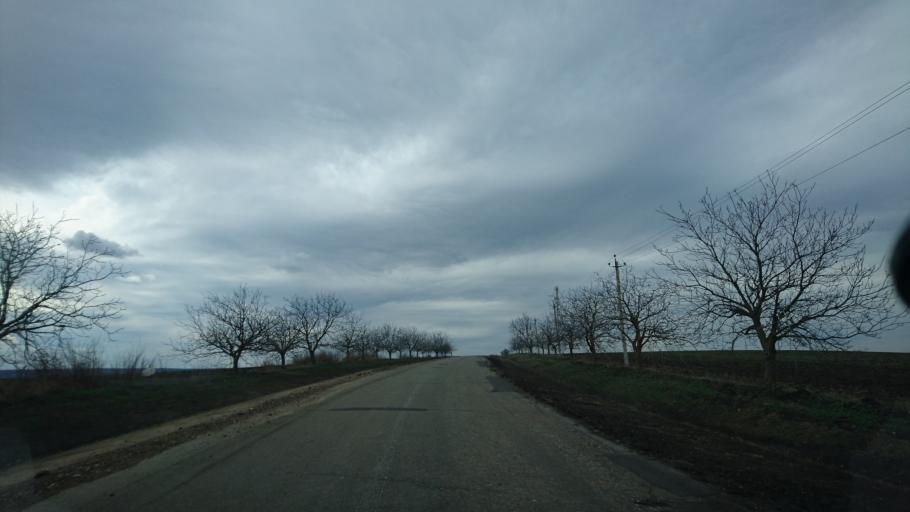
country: MD
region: Cantemir
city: Visniovca
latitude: 46.3259
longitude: 28.4737
